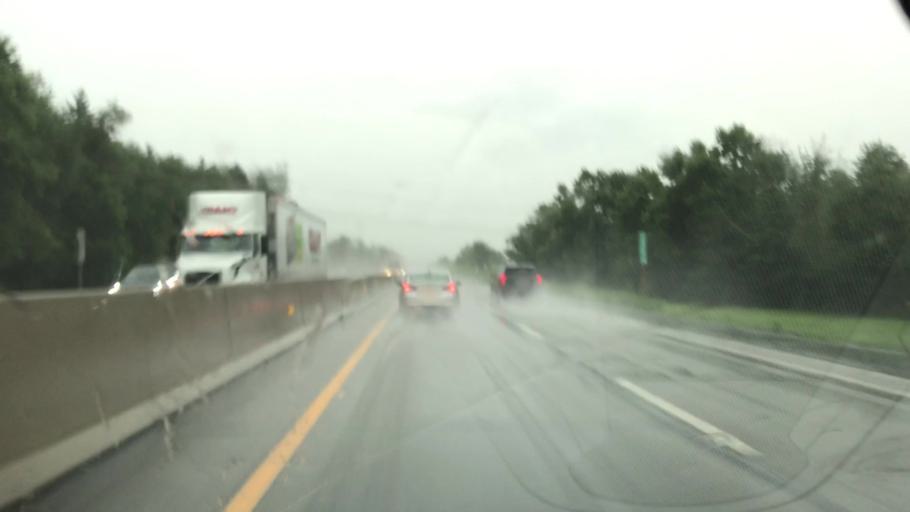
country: US
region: Pennsylvania
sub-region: Cumberland County
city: Boiling Springs
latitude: 40.2201
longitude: -77.0995
